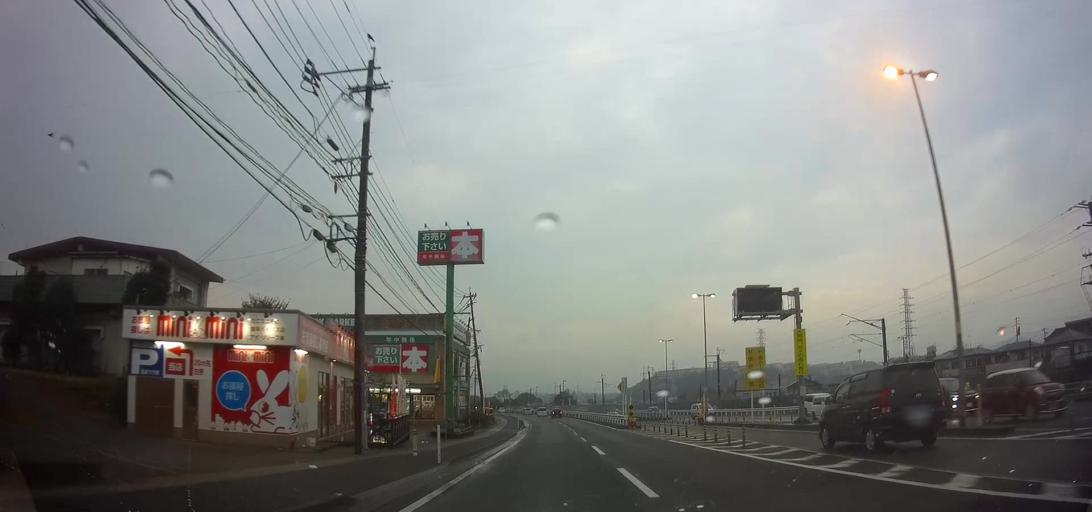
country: JP
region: Nagasaki
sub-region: Isahaya-shi
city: Isahaya
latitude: 32.8413
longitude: 130.0303
